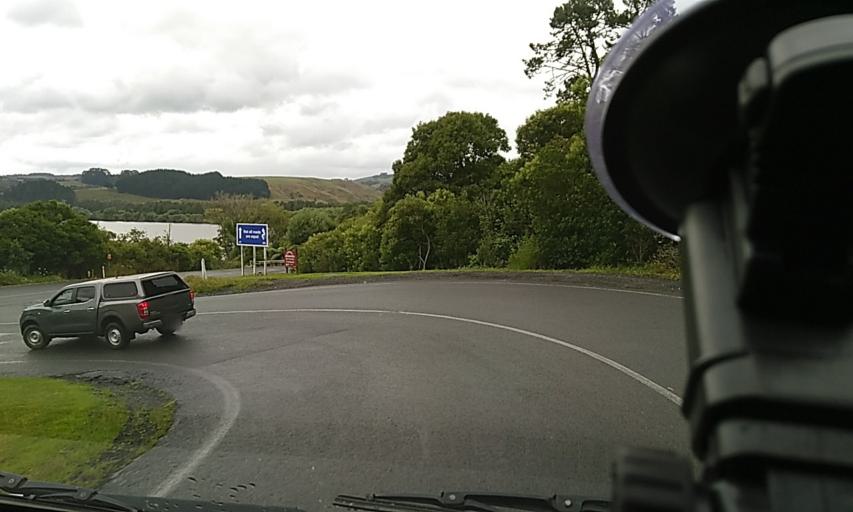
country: NZ
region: Auckland
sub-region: Auckland
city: Pukekohe East
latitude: -37.2995
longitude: 174.9442
